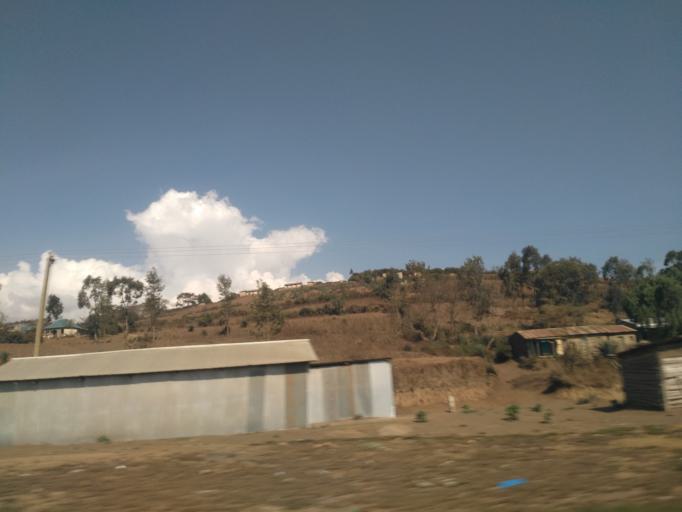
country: TZ
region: Arusha
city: Arusha
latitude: -3.2208
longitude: 36.6062
